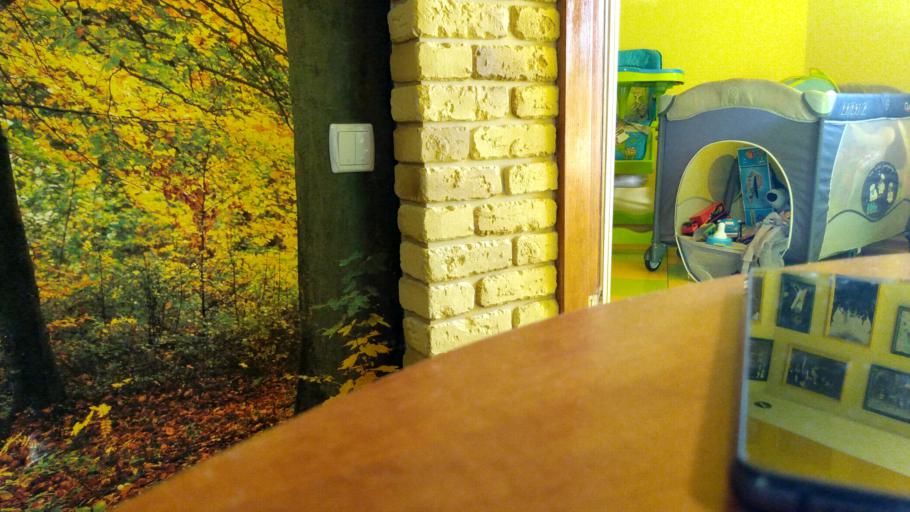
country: RU
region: Tverskaya
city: Kalashnikovo
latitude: 57.2858
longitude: 35.3637
